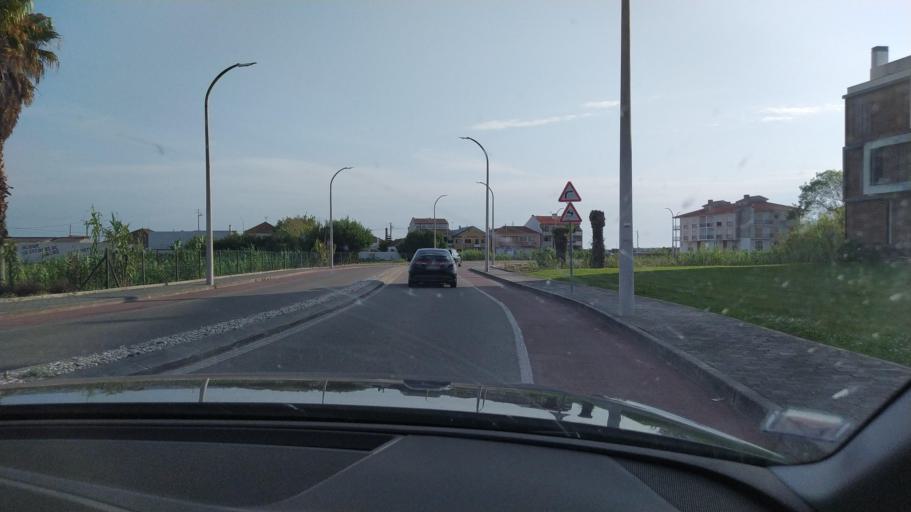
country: PT
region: Aveiro
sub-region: Ilhavo
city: Gafanha da Encarnacao
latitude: 40.5622
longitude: -8.7582
